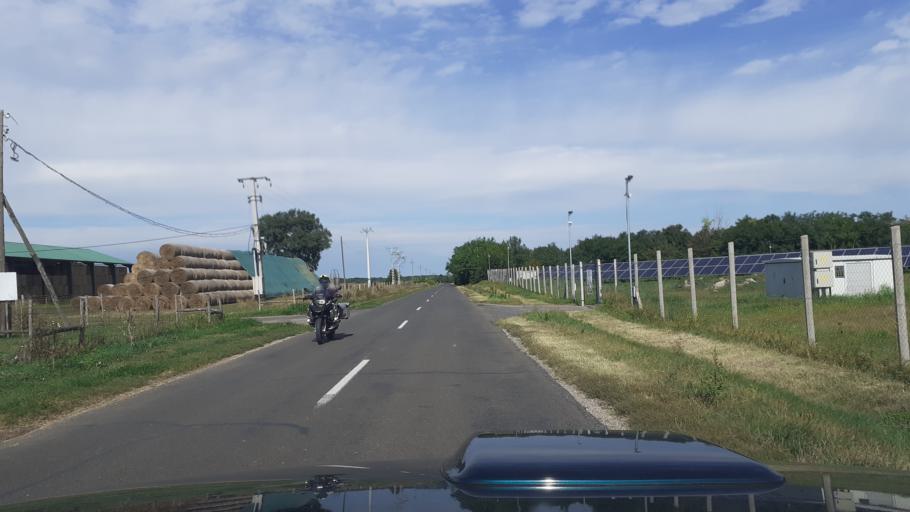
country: HU
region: Fejer
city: Pusztaszabolcs
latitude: 47.1189
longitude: 18.6938
